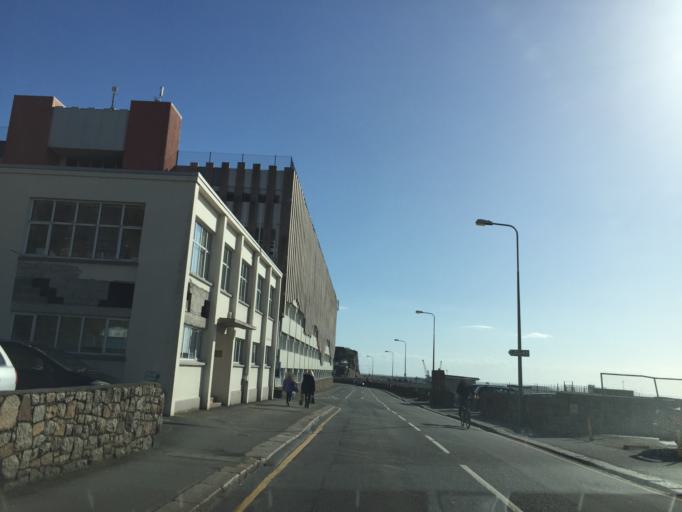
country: JE
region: St Helier
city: Saint Helier
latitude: 49.1813
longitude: -2.1075
